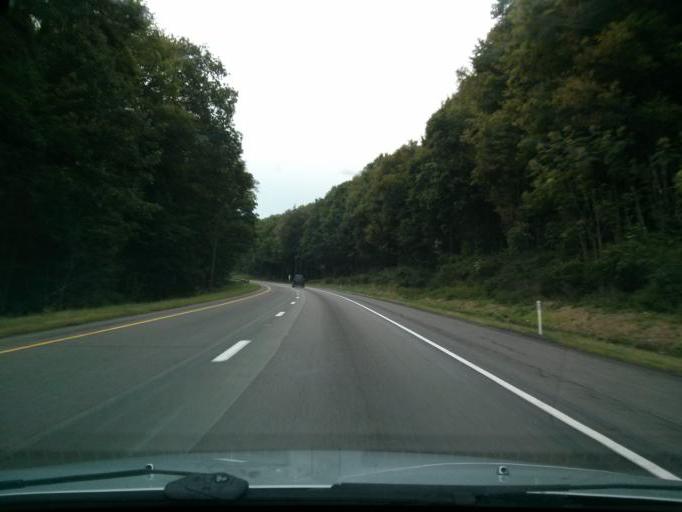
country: US
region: Pennsylvania
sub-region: Jefferson County
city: Brookville
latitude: 41.1483
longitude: -78.9970
